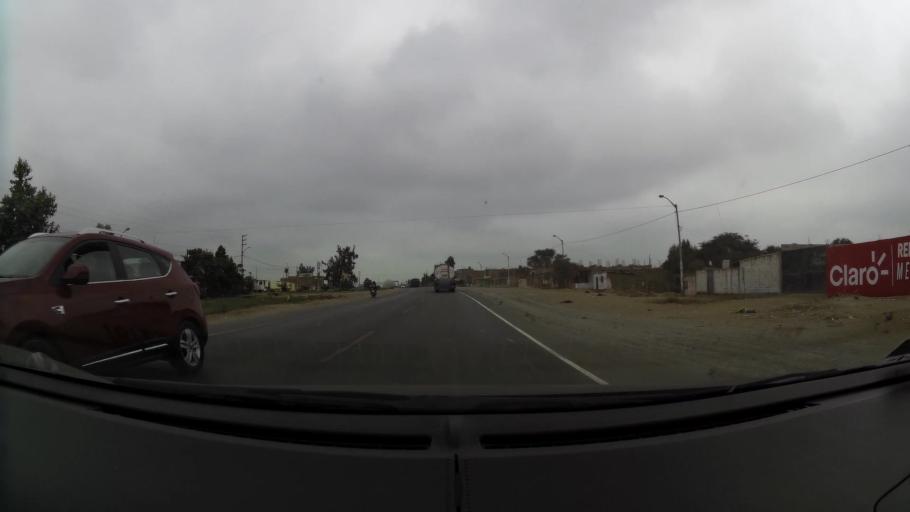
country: PE
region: La Libertad
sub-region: Viru
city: Viru
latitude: -8.4493
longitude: -78.7352
